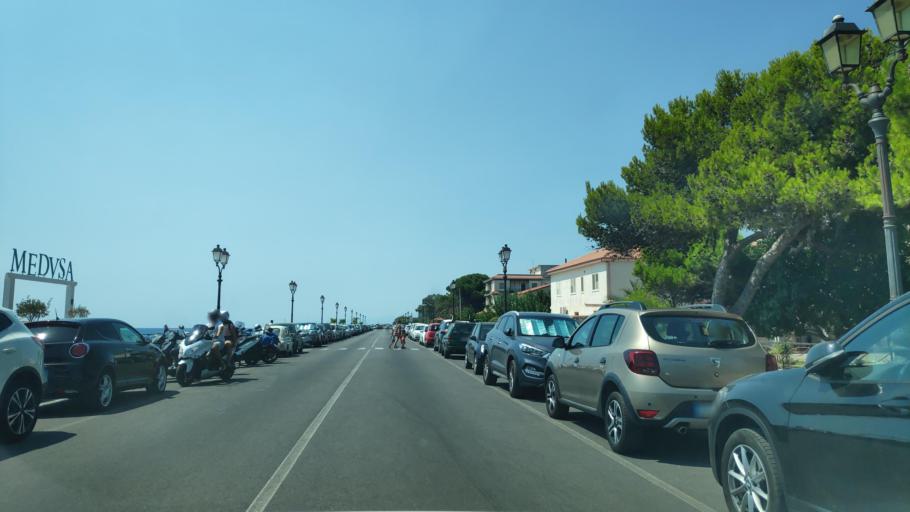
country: IT
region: Calabria
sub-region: Provincia di Reggio Calabria
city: Siderno
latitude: 38.2725
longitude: 16.3045
